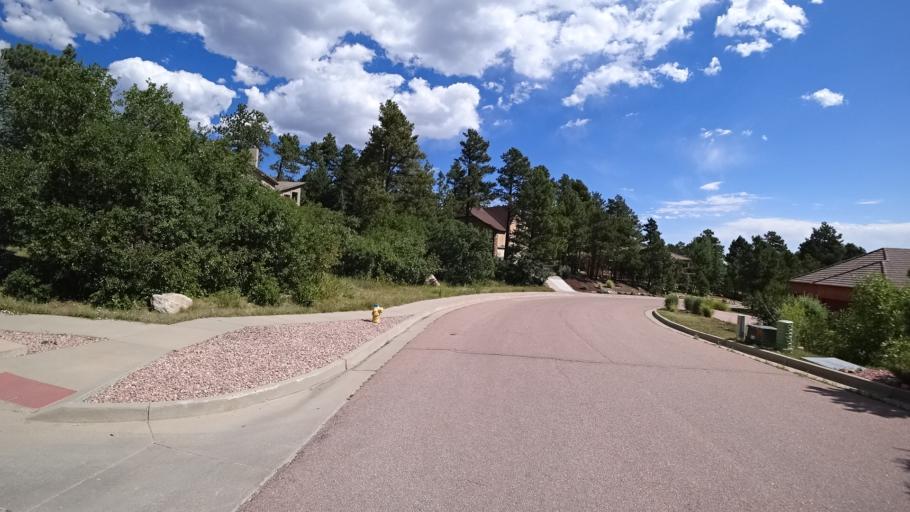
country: US
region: Colorado
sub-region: El Paso County
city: Fort Carson
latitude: 38.7500
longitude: -104.8415
